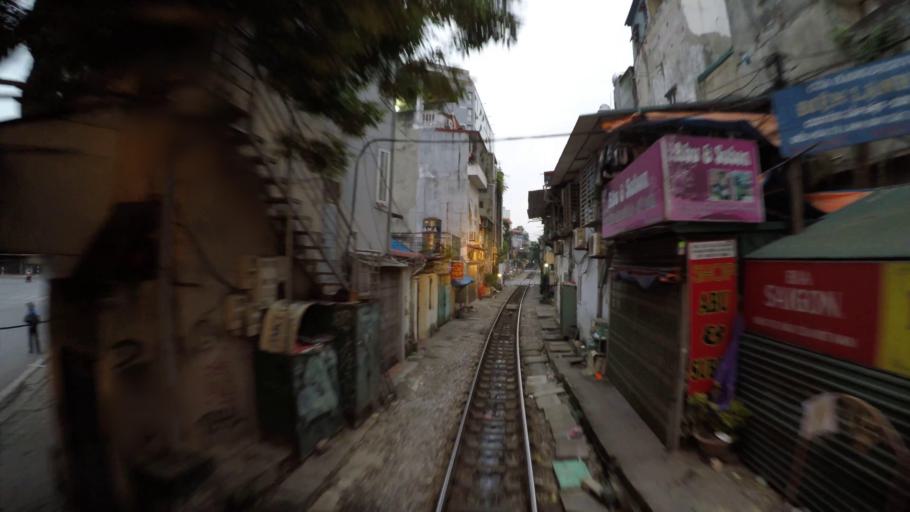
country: VN
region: Ha Noi
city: Hoan Kiem
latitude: 21.0349
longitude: 105.8456
